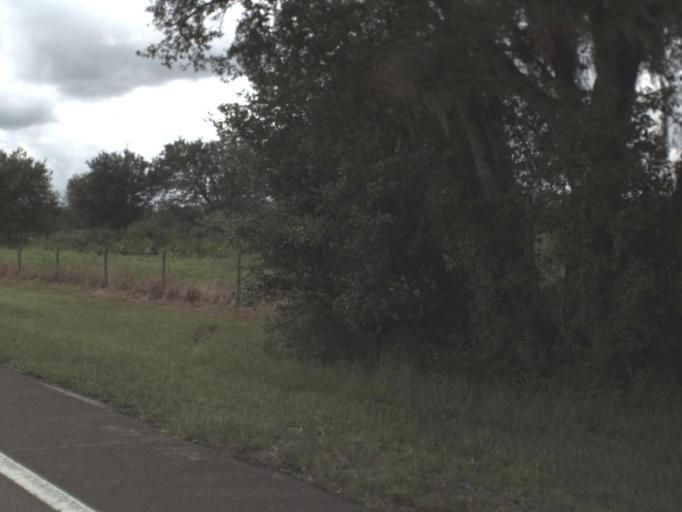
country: US
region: Florida
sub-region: Sarasota County
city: North Port
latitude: 27.1934
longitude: -82.1110
